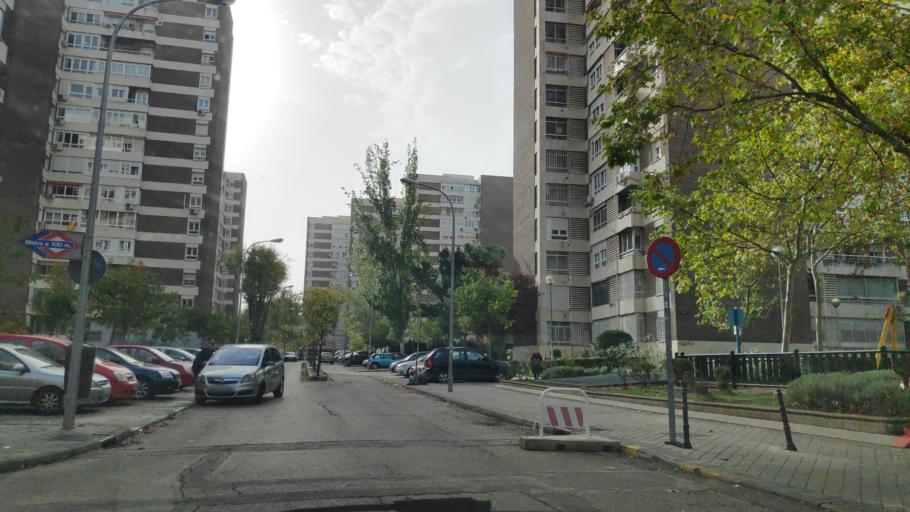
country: ES
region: Madrid
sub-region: Provincia de Madrid
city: Tetuan de las Victorias
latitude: 40.4756
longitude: -3.7040
